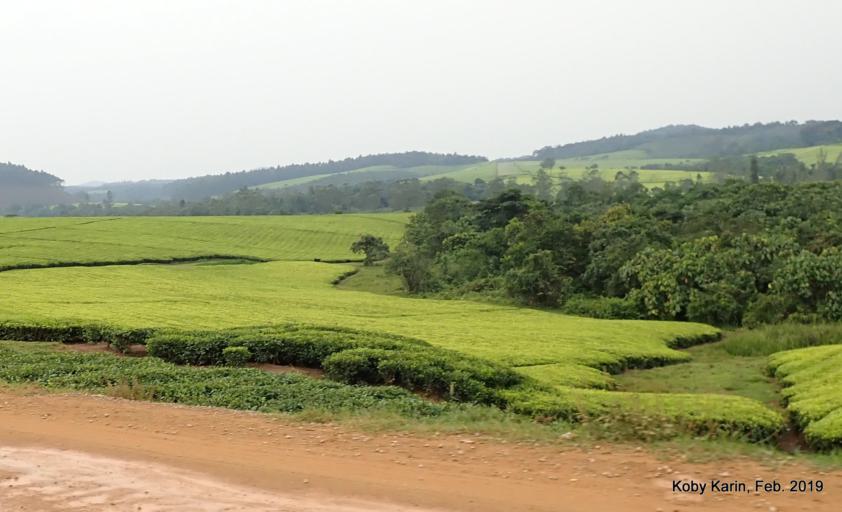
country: UG
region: Western Region
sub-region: Rubirizi District
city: Rubirizi
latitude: -0.3982
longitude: 30.1153
